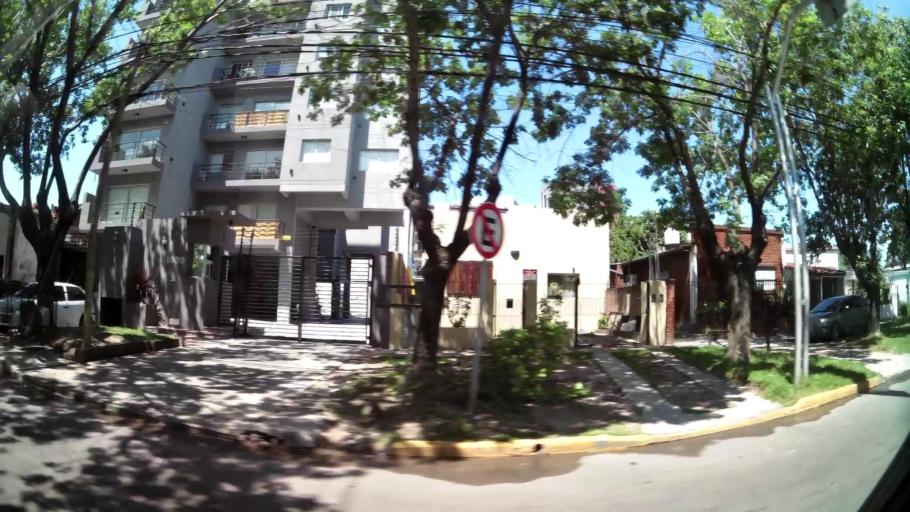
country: AR
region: Buenos Aires
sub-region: Partido de Tigre
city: Tigre
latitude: -34.4302
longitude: -58.5776
